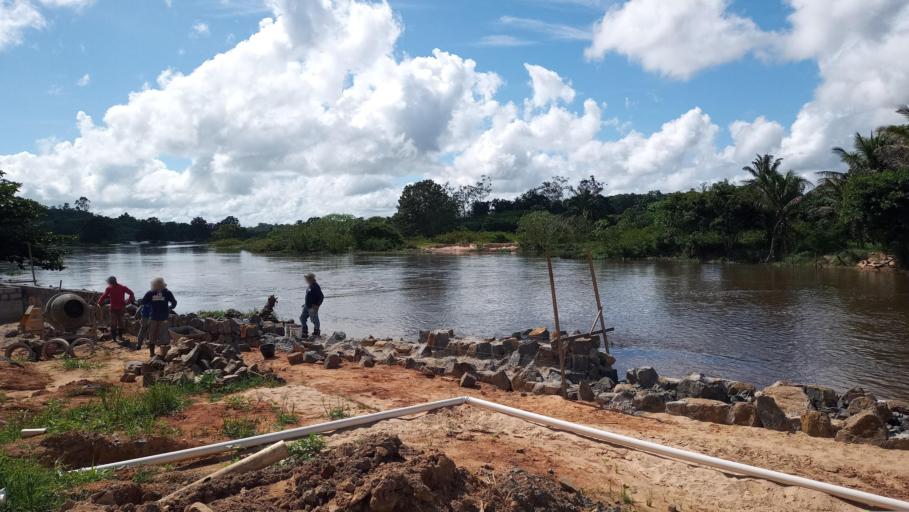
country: BR
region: Bahia
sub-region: Ubata
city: Ubata
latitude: -14.2183
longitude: -39.5172
